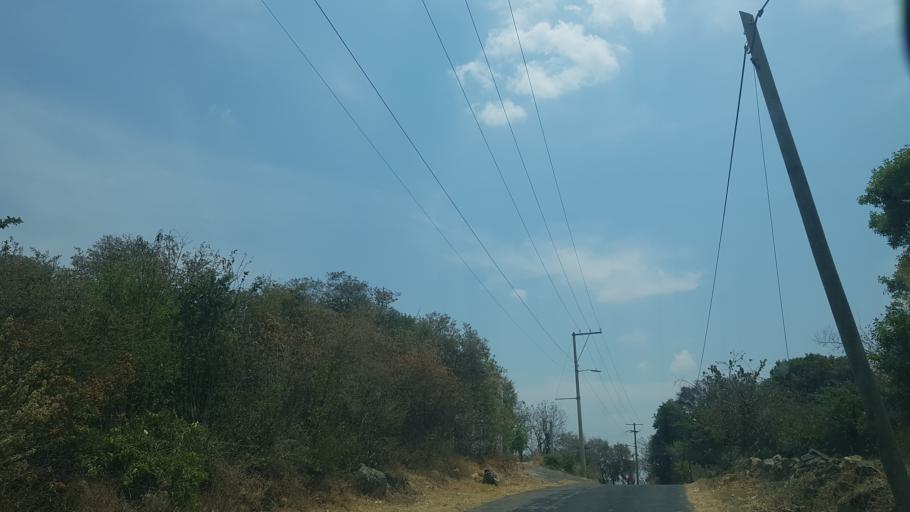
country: MX
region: Puebla
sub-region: Tochimilco
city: La Magdalena Yancuitlalpan
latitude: 18.8874
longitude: -98.6048
